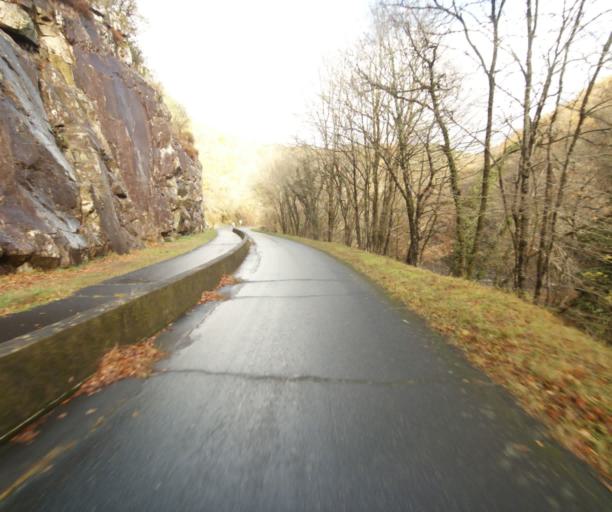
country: FR
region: Limousin
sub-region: Departement de la Correze
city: Cornil
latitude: 45.2159
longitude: 1.6872
